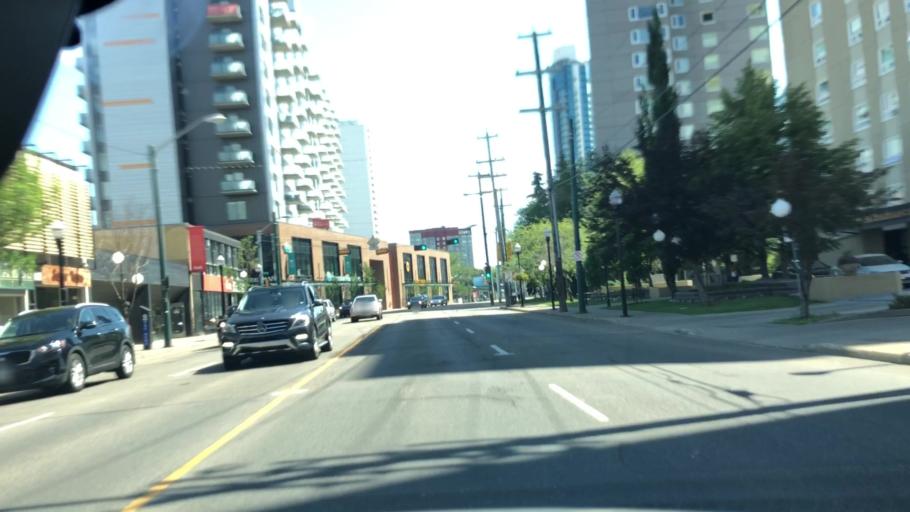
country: CA
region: Alberta
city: Edmonton
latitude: 53.5414
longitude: -113.5353
